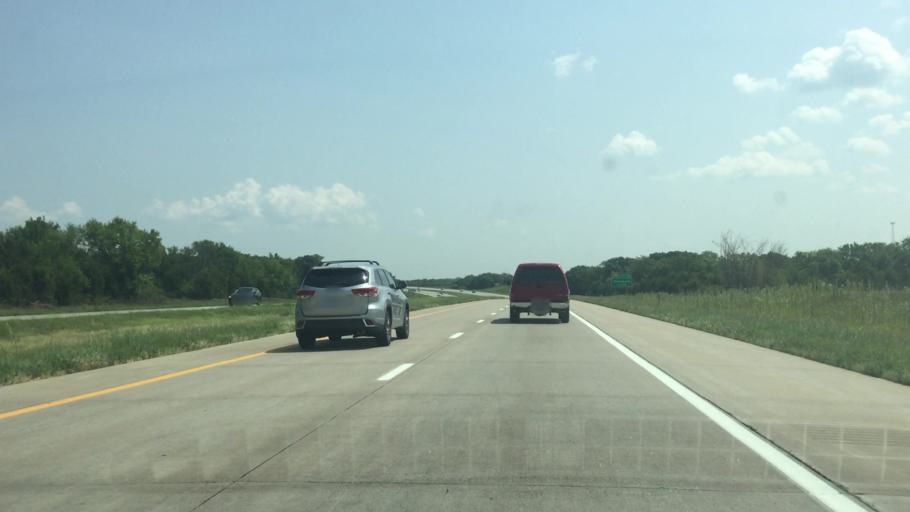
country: US
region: Kansas
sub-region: Franklin County
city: Ottawa
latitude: 38.5298
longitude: -95.3918
